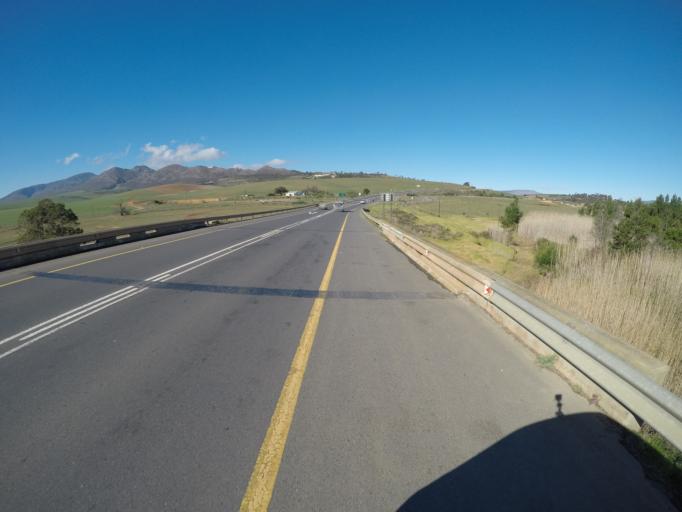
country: ZA
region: Western Cape
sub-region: Overberg District Municipality
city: Caledon
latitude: -34.2103
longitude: 19.3969
